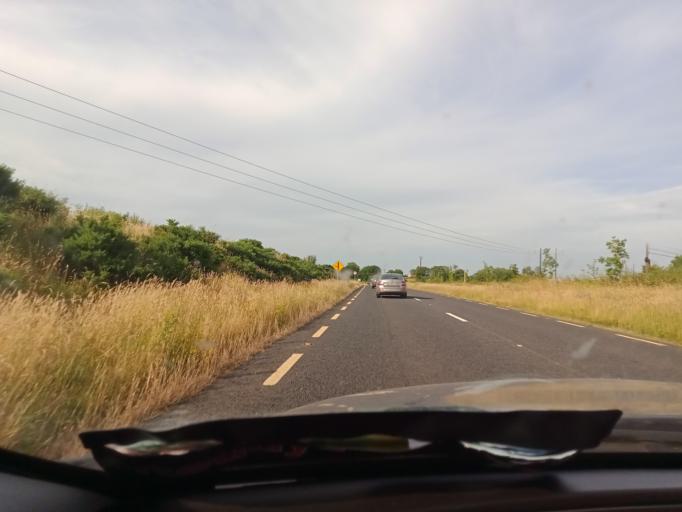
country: IE
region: Ulster
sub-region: An Cabhan
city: Cavan
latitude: 53.9201
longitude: -7.4229
